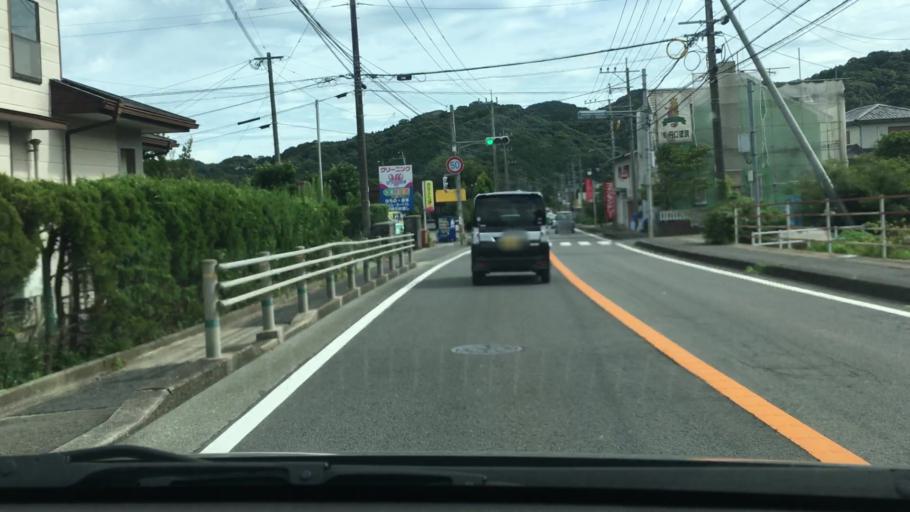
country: JP
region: Nagasaki
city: Togitsu
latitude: 32.8988
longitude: 129.7810
